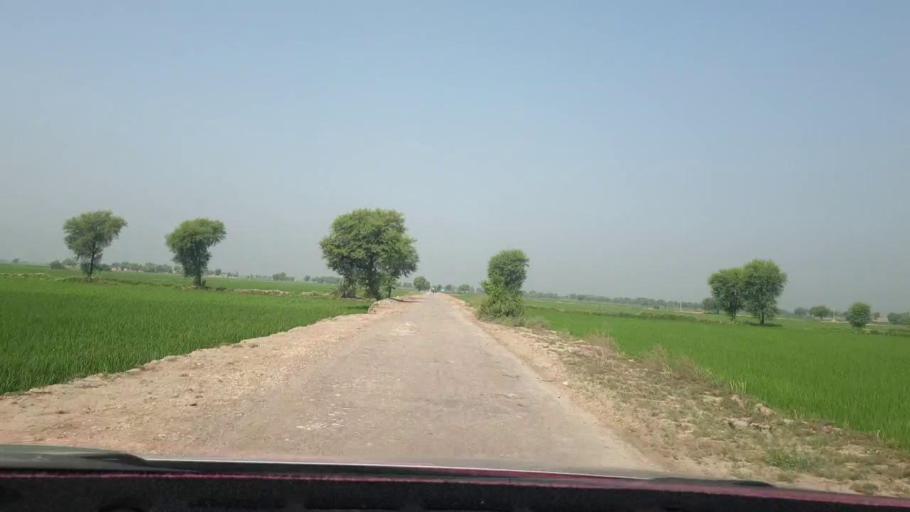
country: PK
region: Sindh
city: Warah
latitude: 27.4308
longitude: 67.8588
